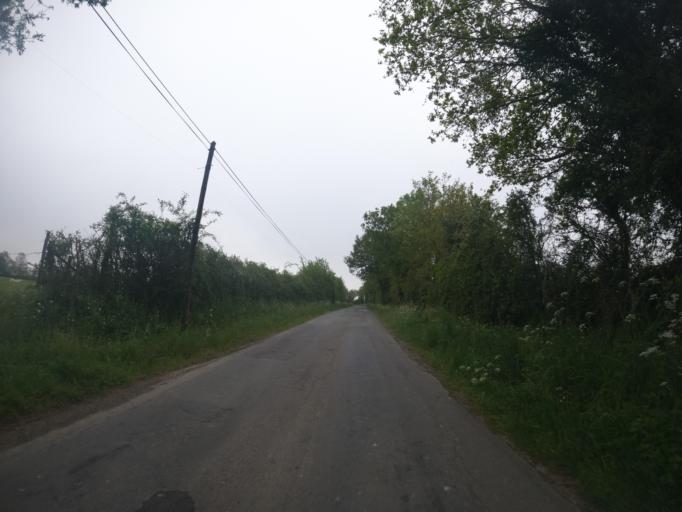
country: FR
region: Poitou-Charentes
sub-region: Departement des Deux-Sevres
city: Chiche
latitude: 46.8913
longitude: -0.3395
